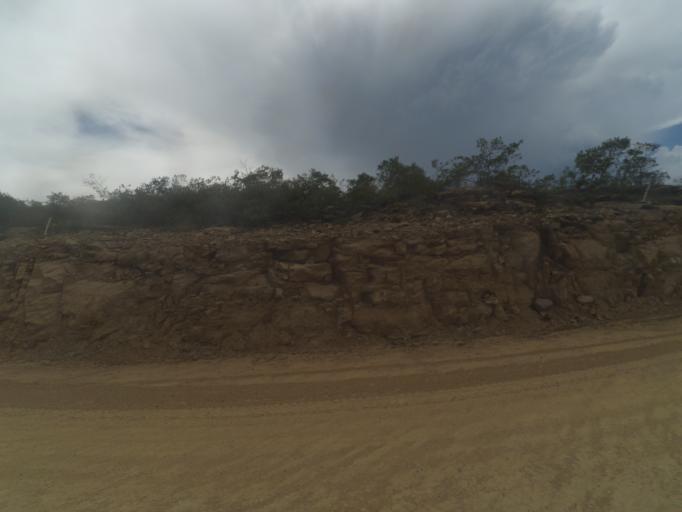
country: BO
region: Chuquisaca
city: Padilla
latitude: -19.3489
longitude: -64.2889
